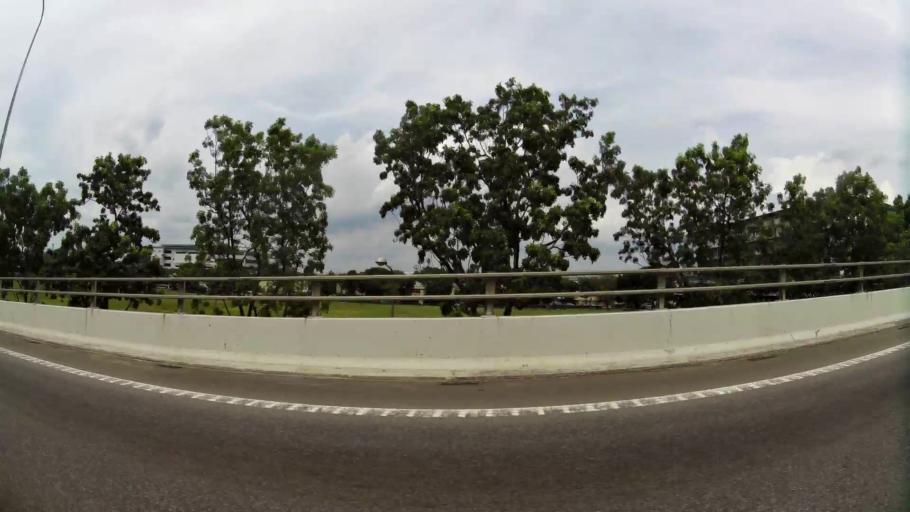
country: MY
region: Johor
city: Johor Bahru
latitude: 1.3228
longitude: 103.6957
